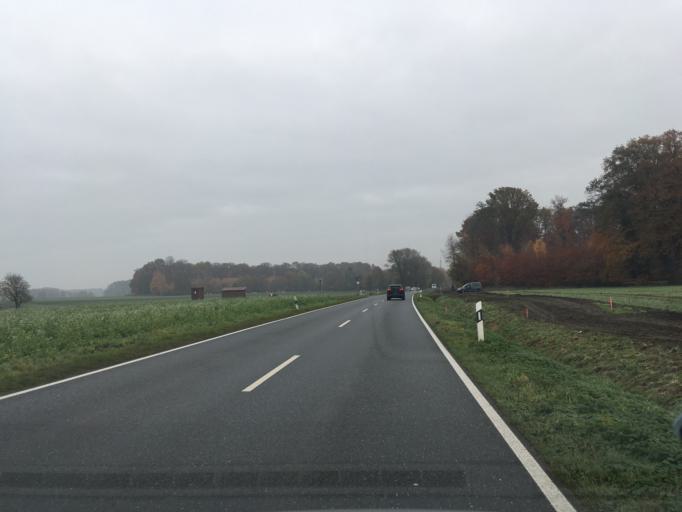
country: DE
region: North Rhine-Westphalia
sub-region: Regierungsbezirk Munster
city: Legden
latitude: 52.0177
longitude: 7.0483
